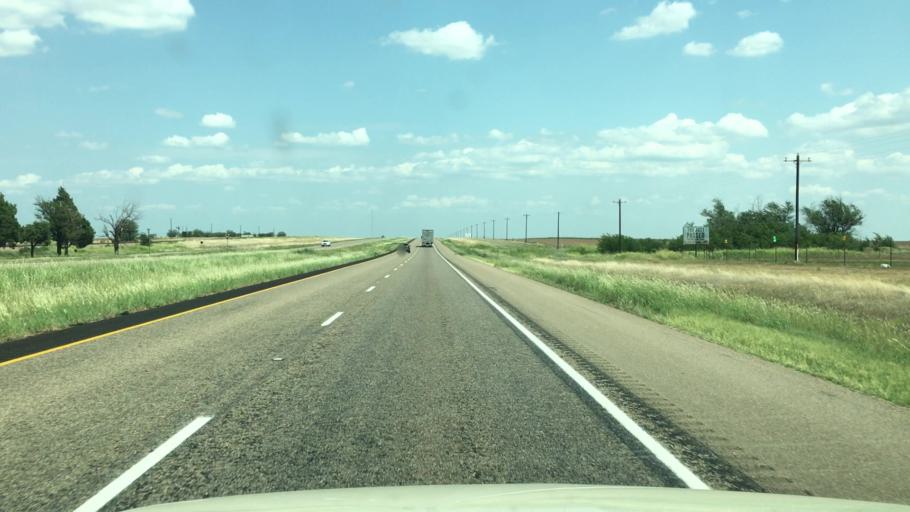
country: US
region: Texas
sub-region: Armstrong County
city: Claude
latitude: 35.0337
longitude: -101.1774
